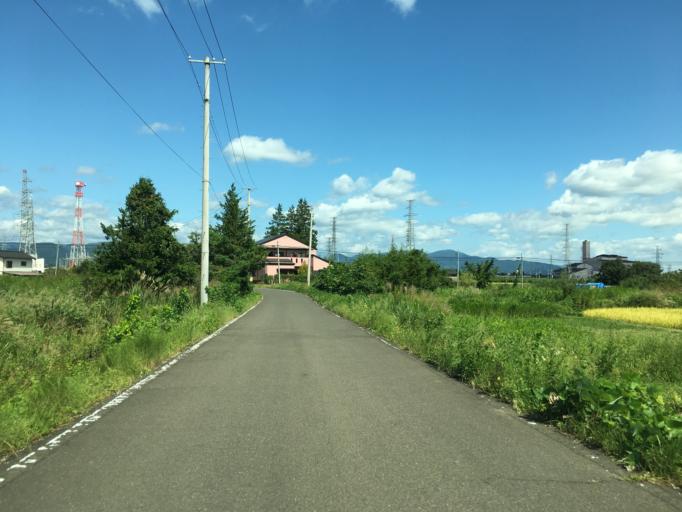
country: JP
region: Fukushima
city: Fukushima-shi
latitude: 37.7456
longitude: 140.4199
